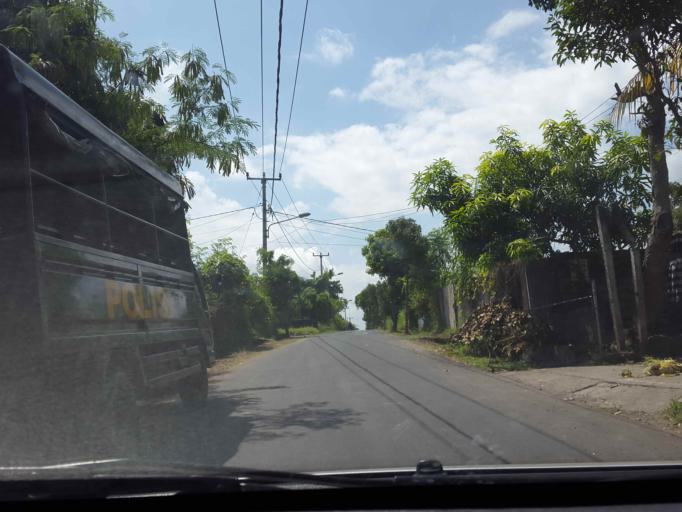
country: ID
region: Bali
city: Semarapura
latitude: -8.5534
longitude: 115.3977
